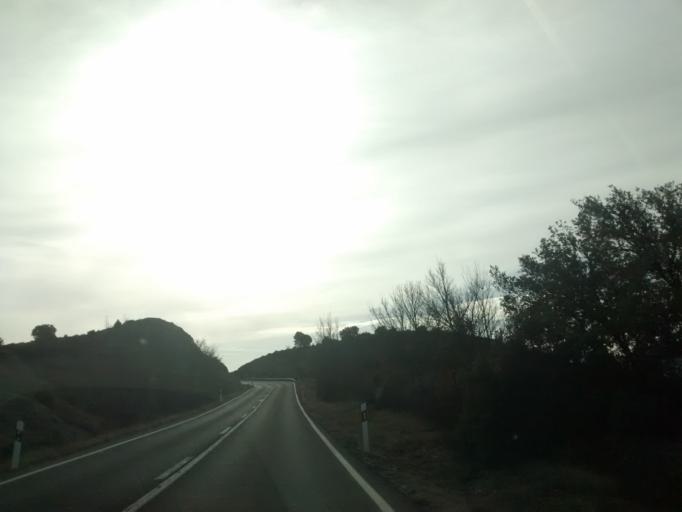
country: ES
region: Aragon
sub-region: Provincia de Zaragoza
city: Mianos
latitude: 42.6042
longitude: -0.8661
